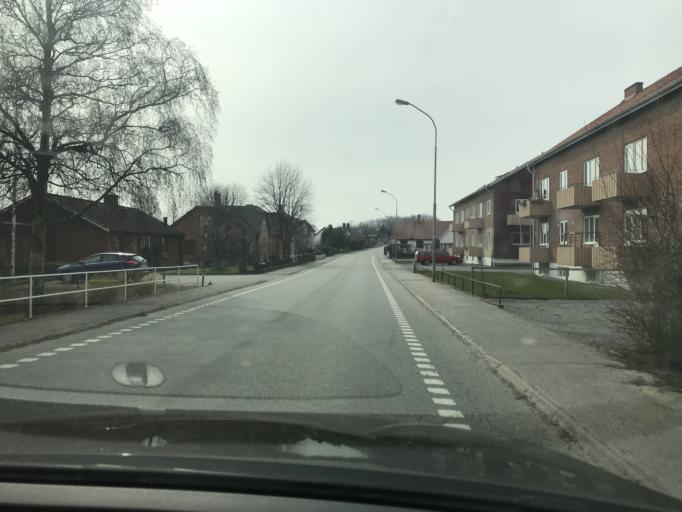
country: SE
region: Skane
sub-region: Skurups Kommun
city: Skivarp
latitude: 55.4240
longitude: 13.5766
